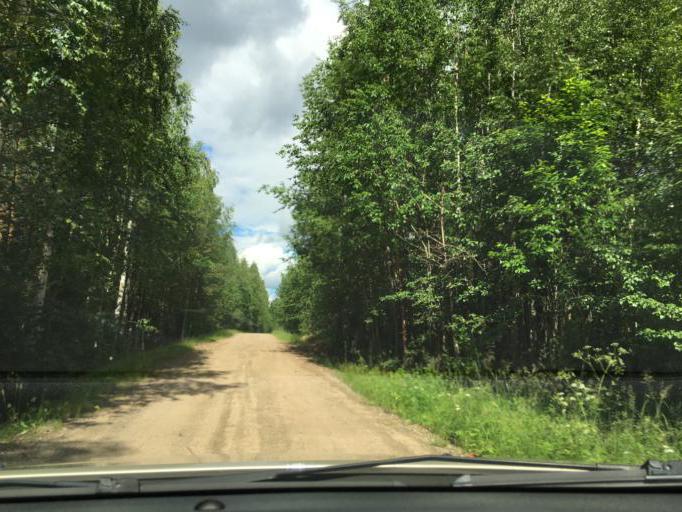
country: SE
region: Norrbotten
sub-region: Overkalix Kommun
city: OEverkalix
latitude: 66.1559
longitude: 22.8586
